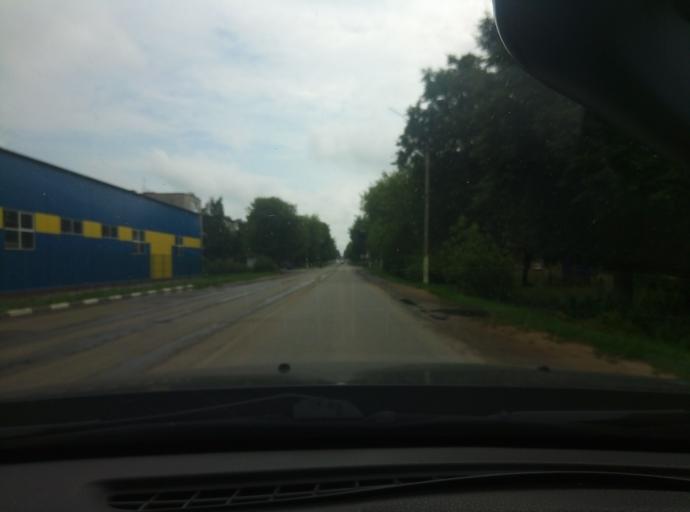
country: RU
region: Tula
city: Kimovsk
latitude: 53.9725
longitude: 38.5089
